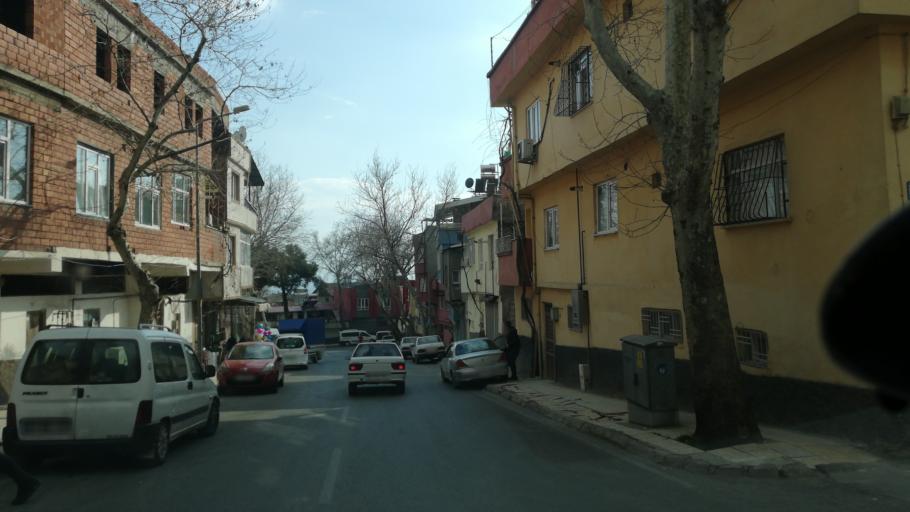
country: TR
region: Kahramanmaras
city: Kahramanmaras
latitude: 37.5855
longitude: 36.9331
